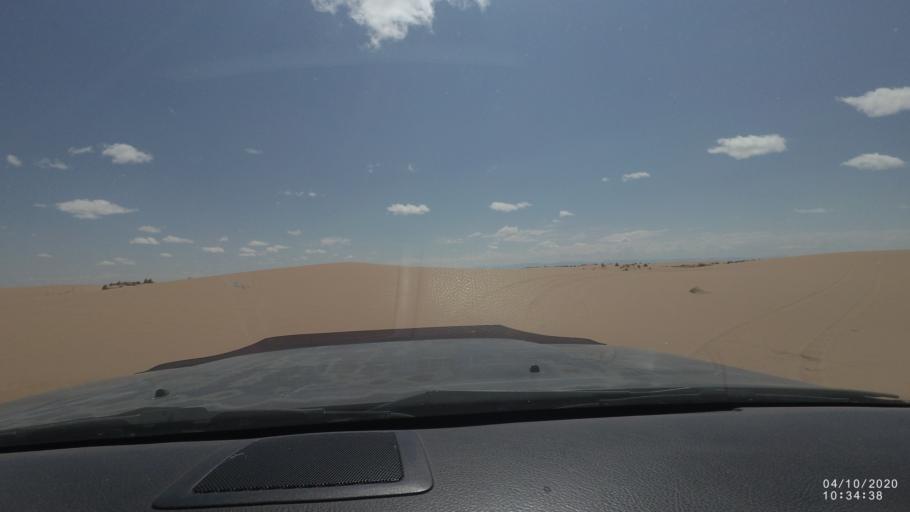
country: BO
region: Oruro
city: Poopo
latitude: -18.7046
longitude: -67.4775
